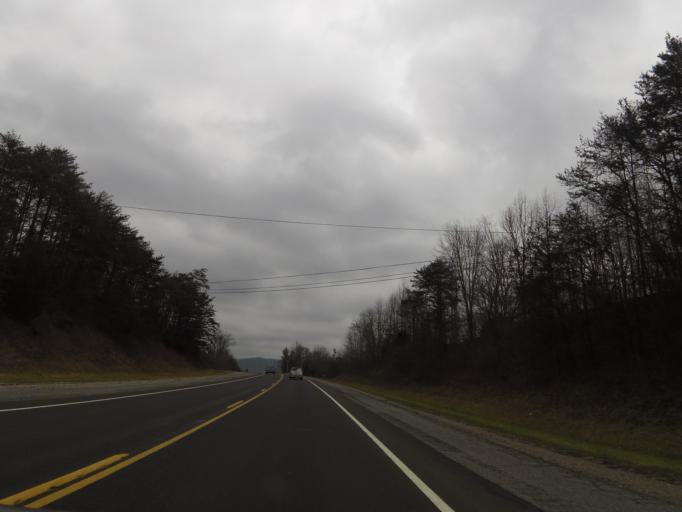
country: US
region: Tennessee
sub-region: Scott County
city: Huntsville
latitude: 36.3788
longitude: -84.3908
